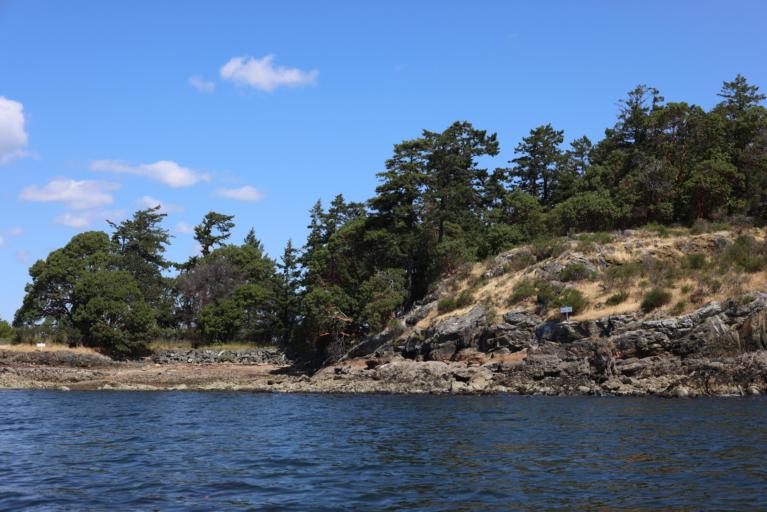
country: CA
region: British Columbia
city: Colwood
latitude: 48.4417
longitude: -123.4378
